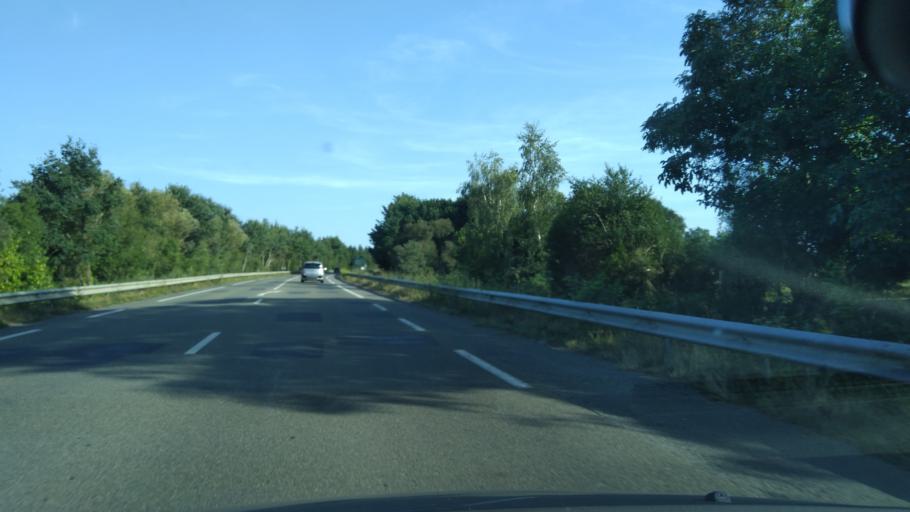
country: FR
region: Pays de la Loire
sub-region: Departement de la Mayenne
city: Entrammes
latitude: 47.9912
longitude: -0.7157
